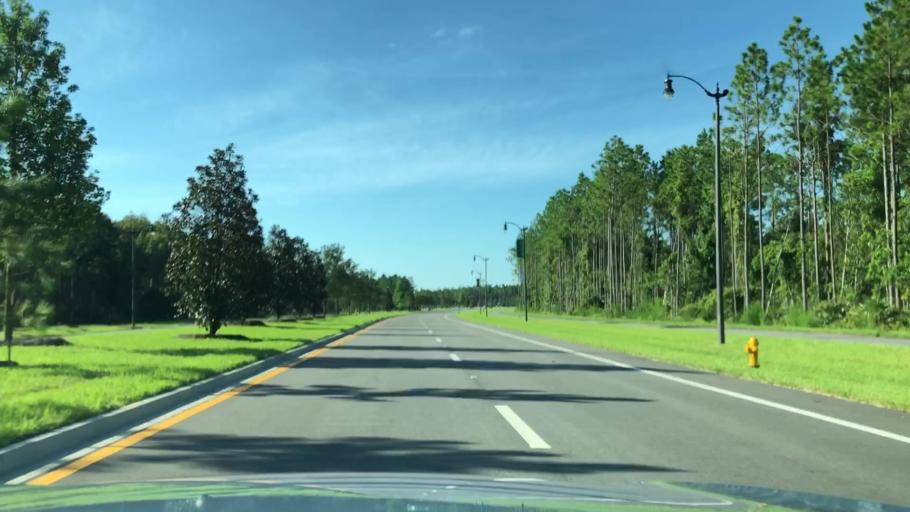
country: US
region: Florida
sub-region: Saint Johns County
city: Palm Valley
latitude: 30.0897
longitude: -81.4063
